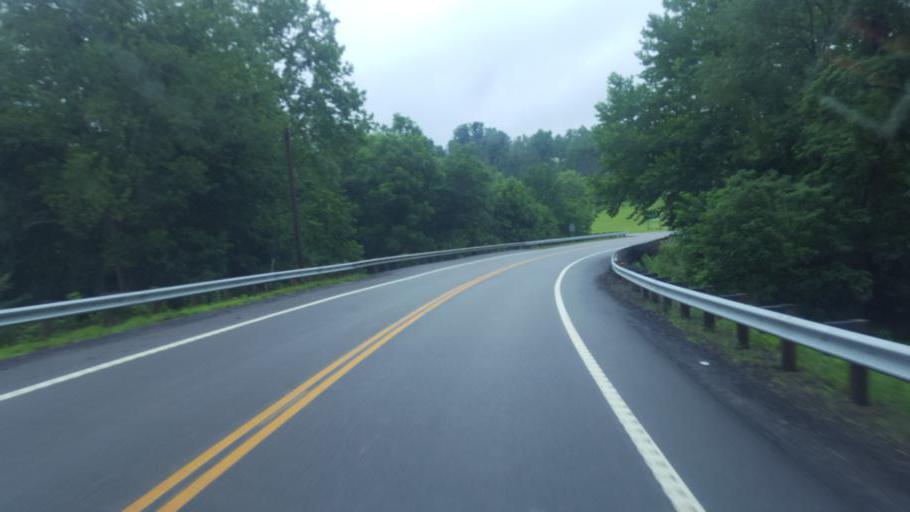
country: US
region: Ohio
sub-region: Columbiana County
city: Salineville
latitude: 40.5097
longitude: -80.8958
